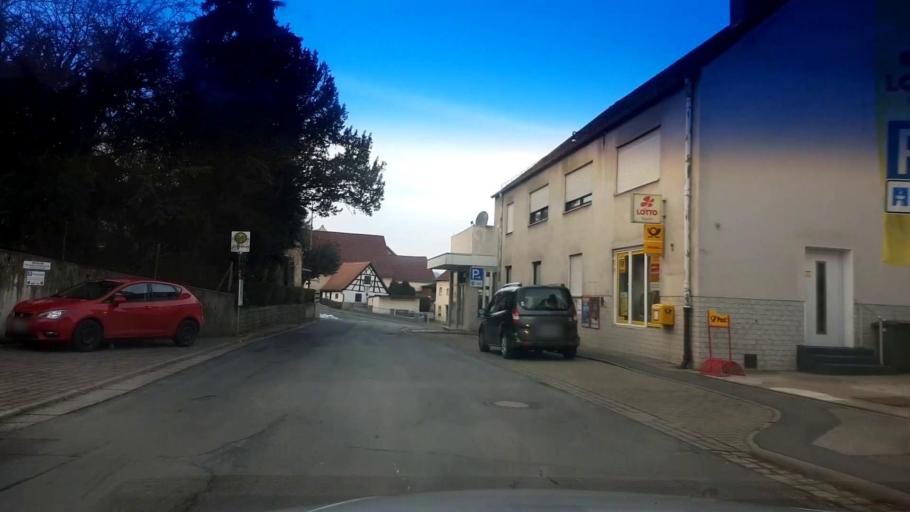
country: DE
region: Bavaria
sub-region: Upper Franconia
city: Hirschaid
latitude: 49.8073
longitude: 10.9819
